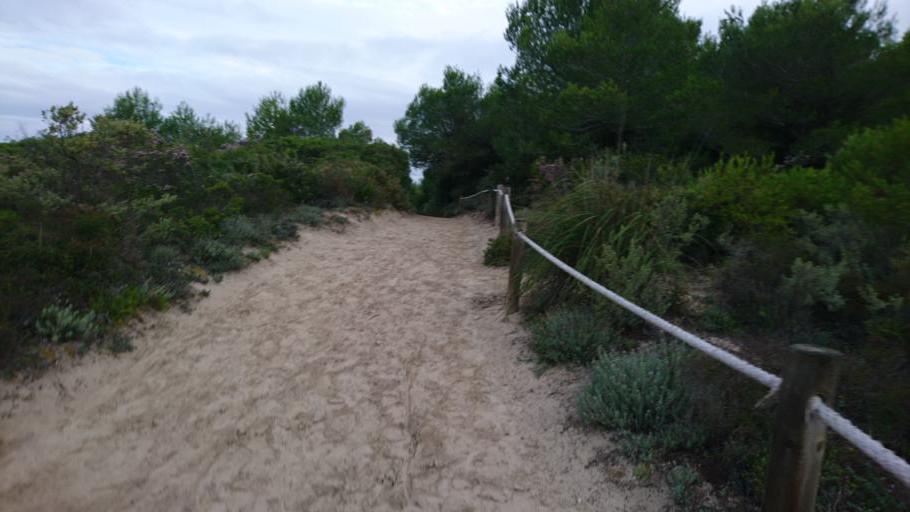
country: ES
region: Balearic Islands
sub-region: Illes Balears
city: Port d'Alcudia
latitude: 39.7766
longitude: 3.1385
